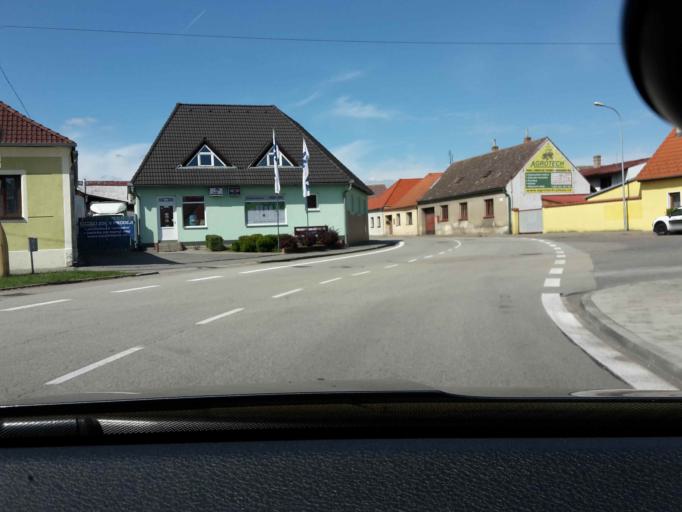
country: CZ
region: Jihocesky
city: Kardasova Recice
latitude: 49.1848
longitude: 14.8511
